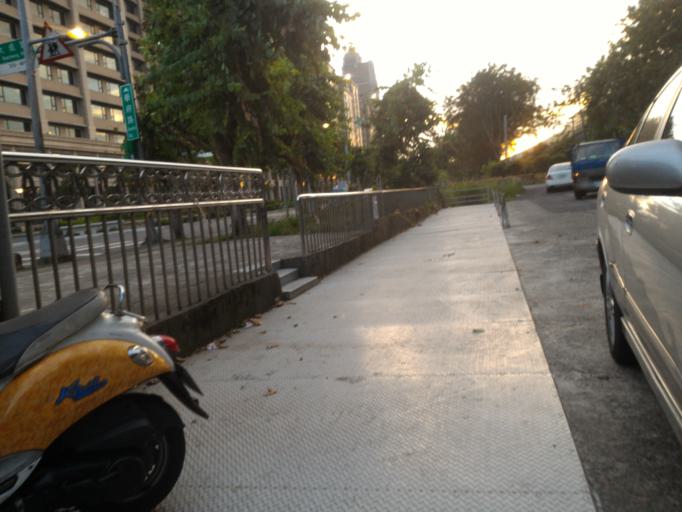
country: TW
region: Taiwan
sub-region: Taoyuan
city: Taoyuan
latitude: 24.9512
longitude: 121.3814
